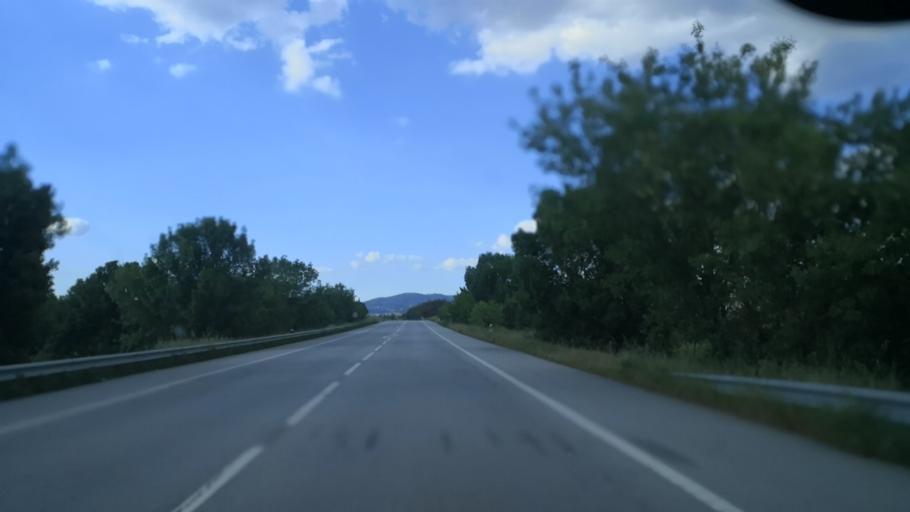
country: PT
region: Portalegre
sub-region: Portalegre
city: Urra
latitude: 39.2430
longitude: -7.4505
